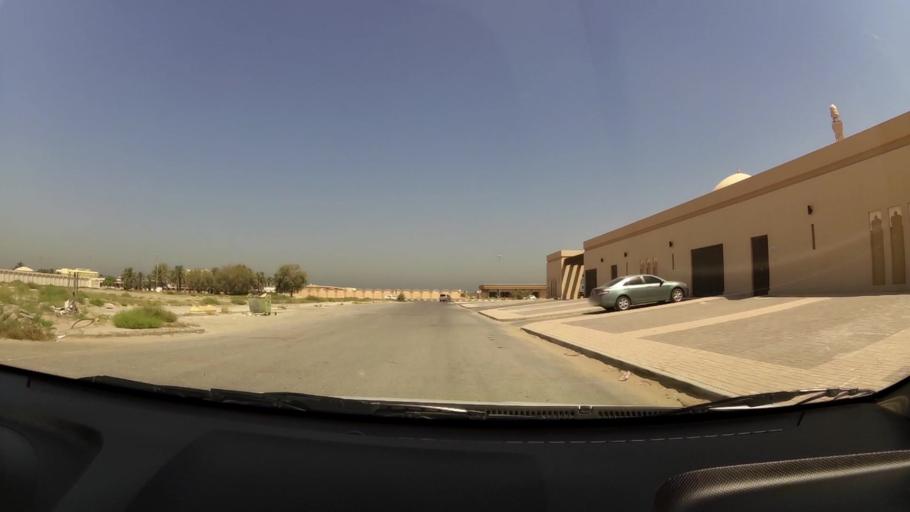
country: AE
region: Umm al Qaywayn
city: Umm al Qaywayn
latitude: 25.5611
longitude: 55.5476
